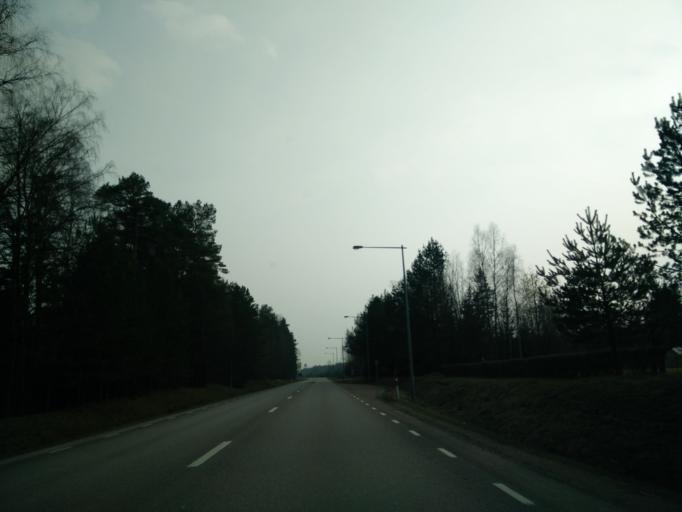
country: SE
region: Vaermland
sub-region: Forshaga Kommun
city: Forshaga
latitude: 59.5120
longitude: 13.4398
